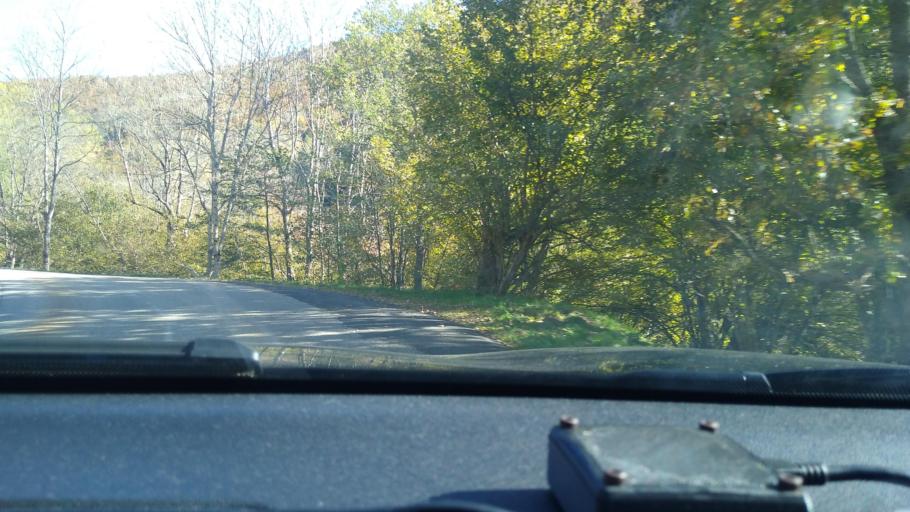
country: FR
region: Midi-Pyrenees
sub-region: Departement de l'Ariege
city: Ax-les-Thermes
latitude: 42.7195
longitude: 1.8756
